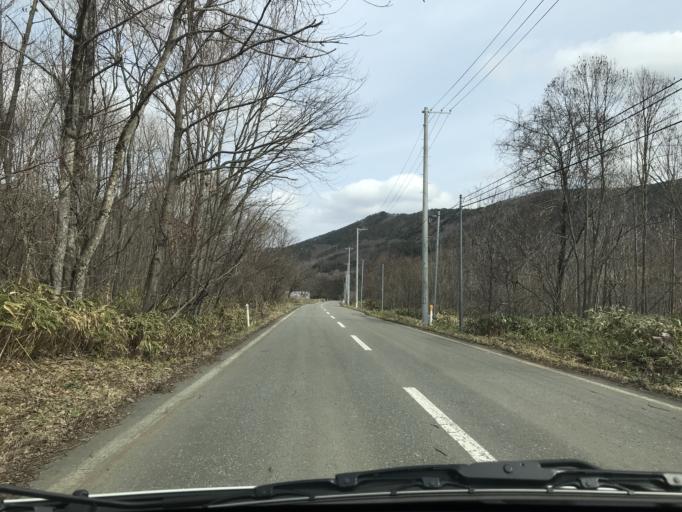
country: JP
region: Iwate
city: Kitakami
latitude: 39.2636
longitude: 141.3178
